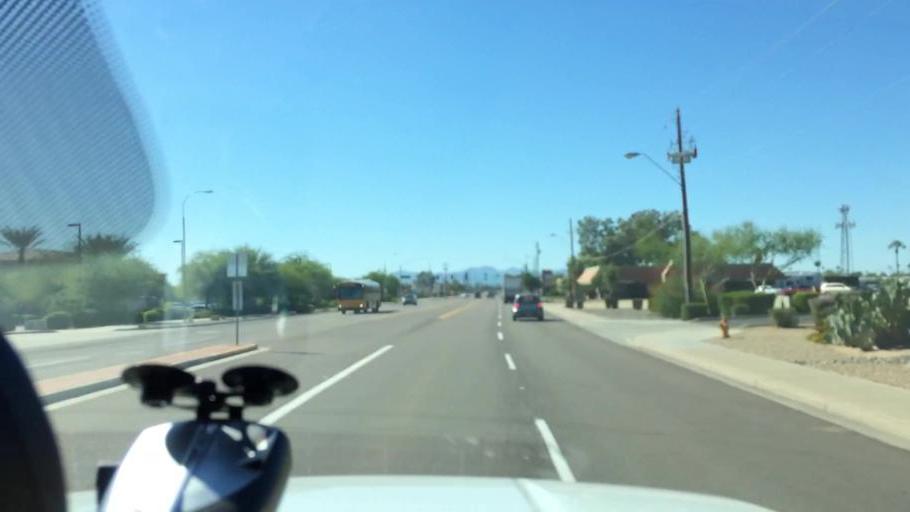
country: US
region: Arizona
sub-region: Maricopa County
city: Sun City
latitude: 33.5812
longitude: -112.2618
